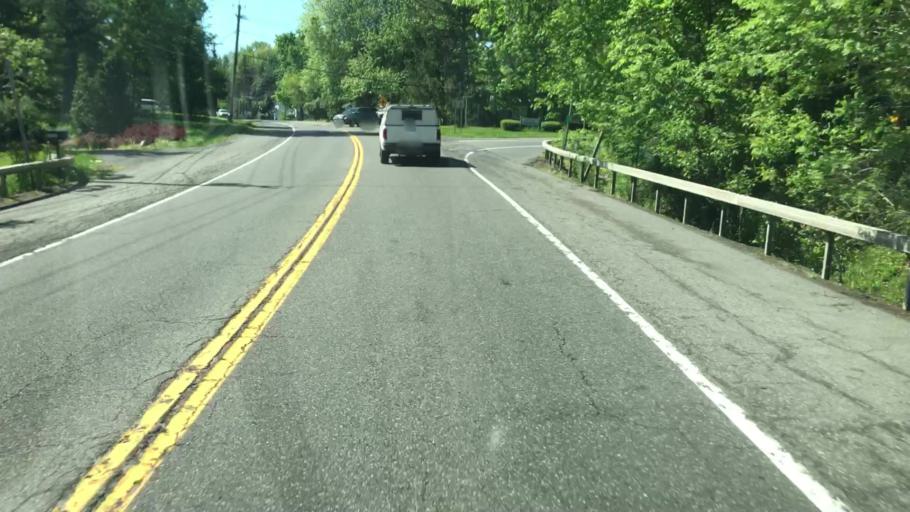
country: US
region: New York
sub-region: Onondaga County
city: Seneca Knolls
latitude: 43.1318
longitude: -76.2548
